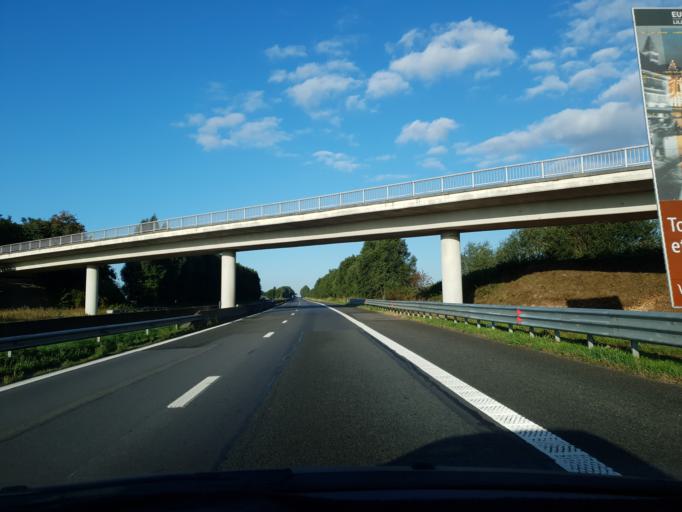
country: BE
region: Wallonia
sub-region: Province du Hainaut
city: Frasnes-lez-Buissenal
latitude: 50.6634
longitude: 3.5396
